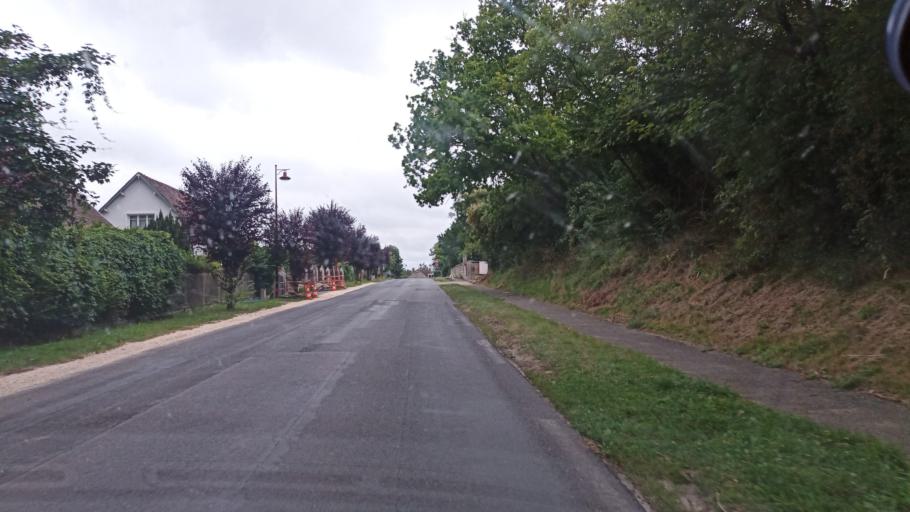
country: FR
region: Ile-de-France
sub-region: Departement de Seine-et-Marne
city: Voulx
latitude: 48.2848
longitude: 2.9640
